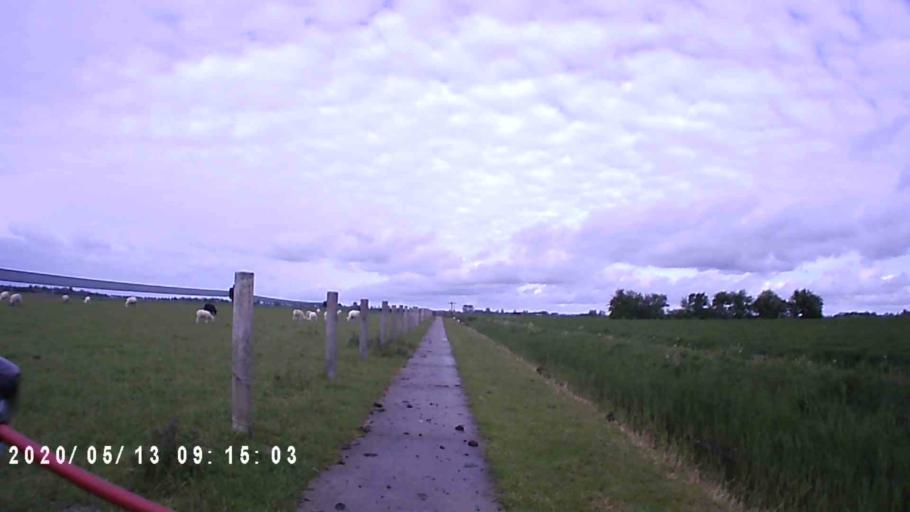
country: NL
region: Groningen
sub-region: Gemeente Zuidhorn
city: Noordhorn
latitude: 53.2736
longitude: 6.4140
